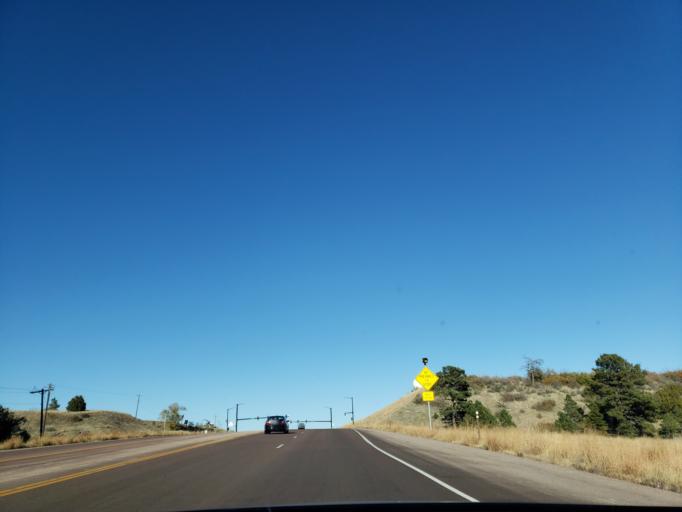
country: US
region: Colorado
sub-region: El Paso County
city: Fort Carson
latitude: 38.7001
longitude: -104.8290
